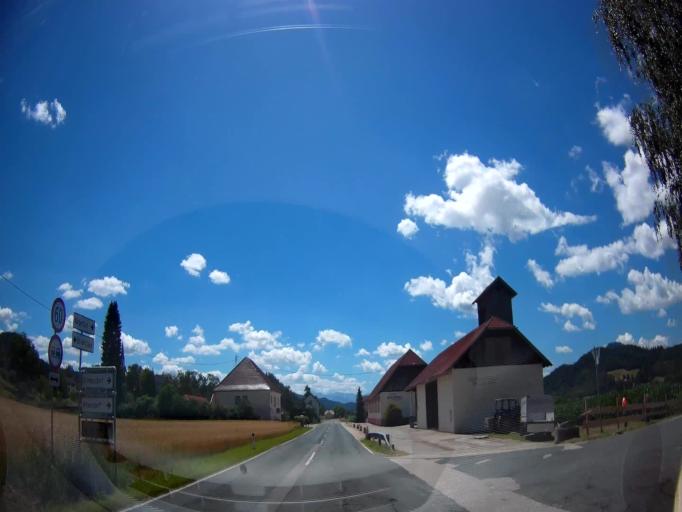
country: AT
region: Carinthia
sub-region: Politischer Bezirk Sankt Veit an der Glan
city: Sankt Veit an der Glan
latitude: 46.7217
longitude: 14.3785
